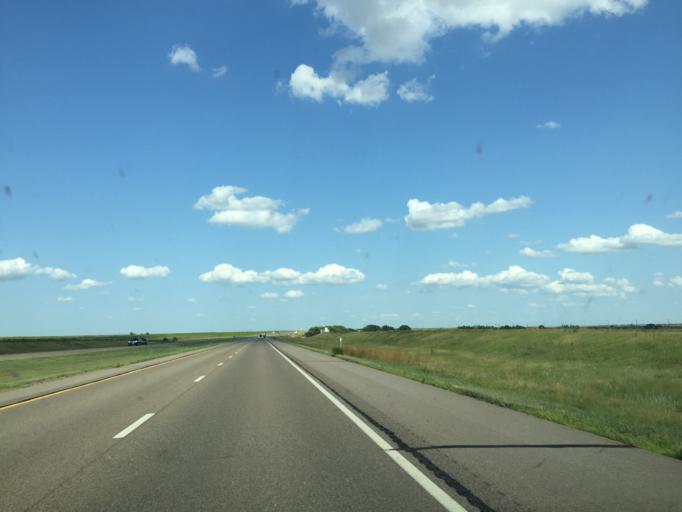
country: US
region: Kansas
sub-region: Trego County
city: WaKeeney
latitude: 39.0231
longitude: -100.0122
